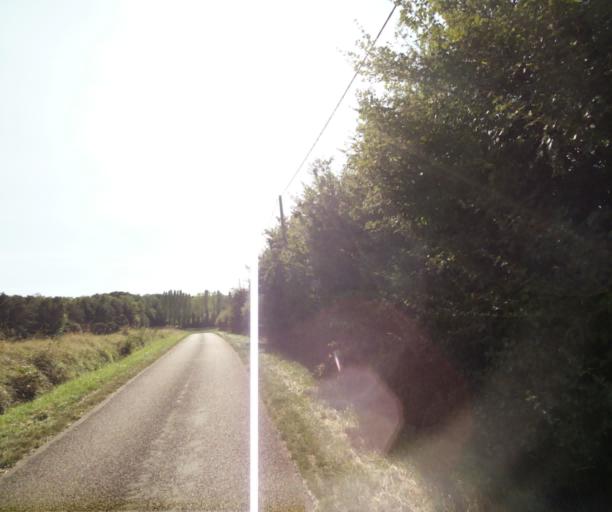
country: FR
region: Bourgogne
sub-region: Departement de Saone-et-Loire
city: Tournus
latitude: 46.5517
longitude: 4.8773
